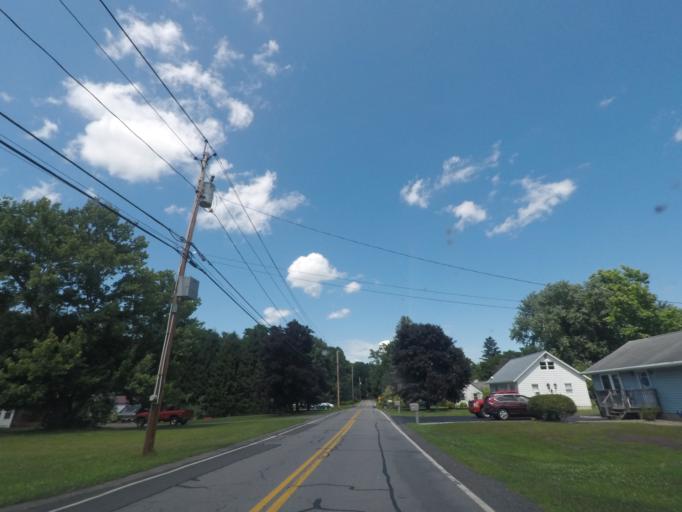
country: US
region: New York
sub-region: Schenectady County
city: Rotterdam
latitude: 42.7441
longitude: -73.9447
